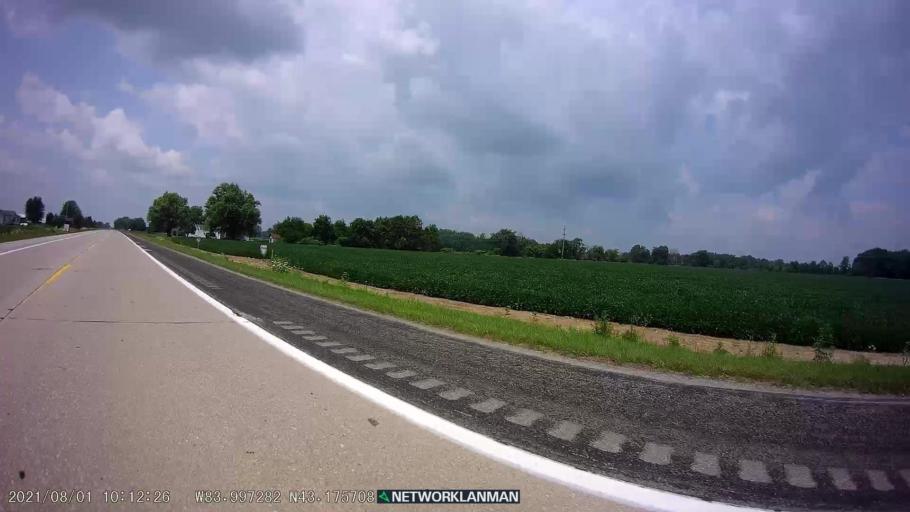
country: US
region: Michigan
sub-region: Genesee County
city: Montrose
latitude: 43.1758
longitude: -83.9976
